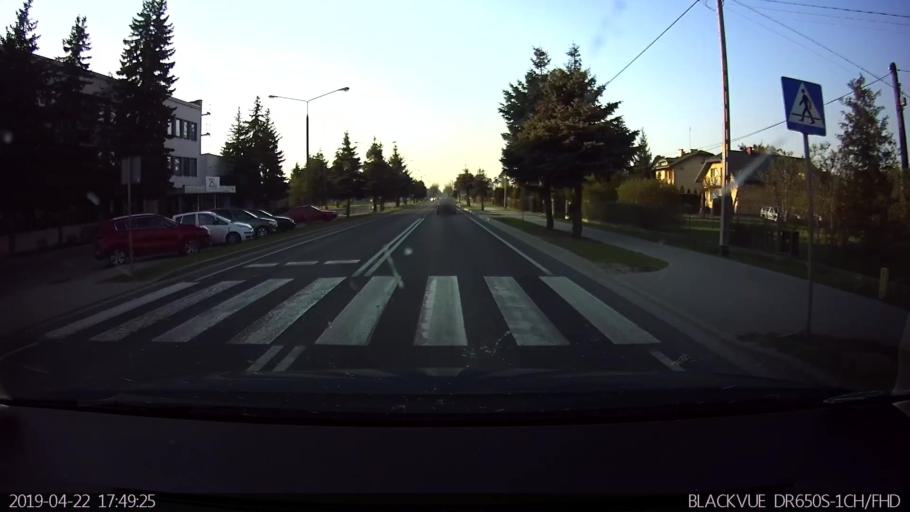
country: PL
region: Masovian Voivodeship
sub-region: Powiat wegrowski
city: Wegrow
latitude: 52.4138
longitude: 22.0089
